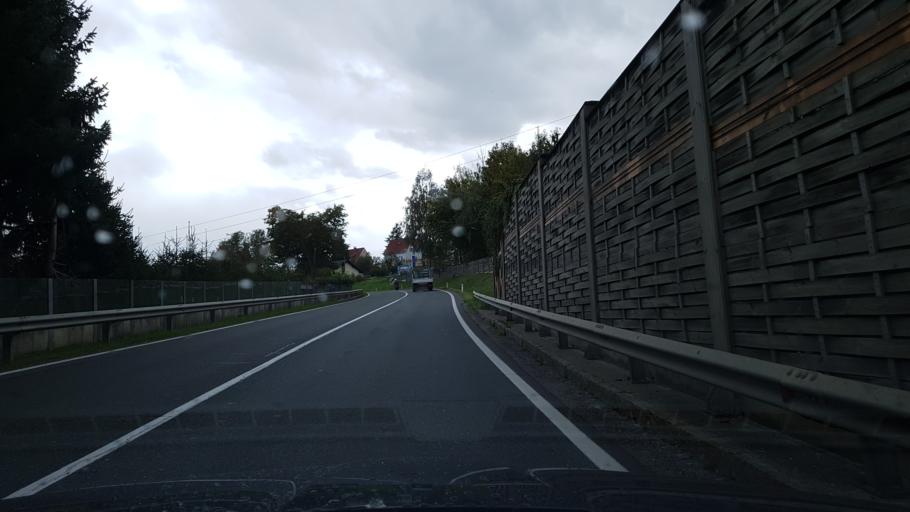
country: AT
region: Styria
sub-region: Politischer Bezirk Voitsberg
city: Koflach
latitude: 47.0633
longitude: 15.0734
